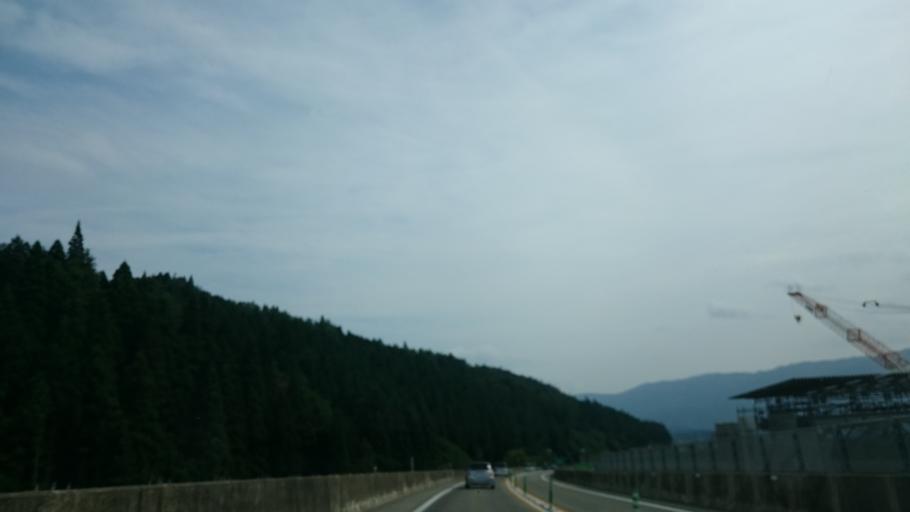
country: JP
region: Gifu
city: Gujo
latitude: 35.8868
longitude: 136.8862
